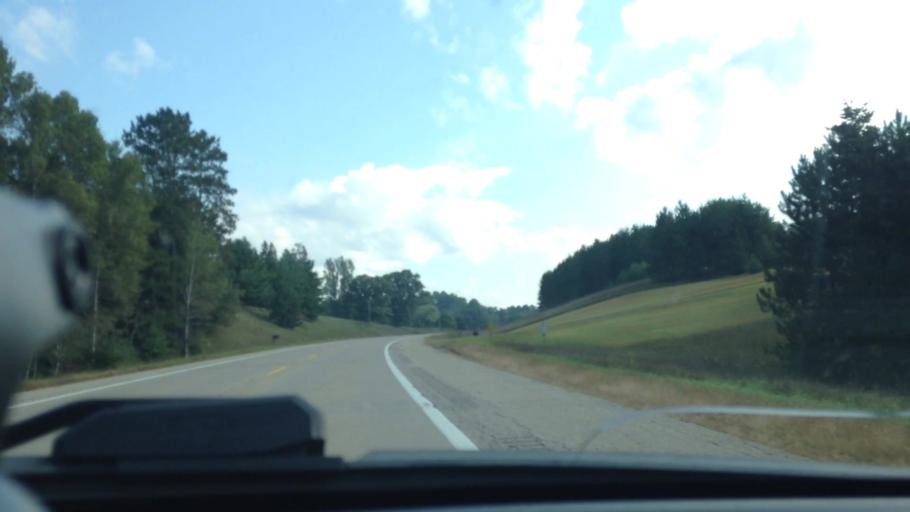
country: US
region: Michigan
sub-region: Dickinson County
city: Norway
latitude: 45.7636
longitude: -87.9193
